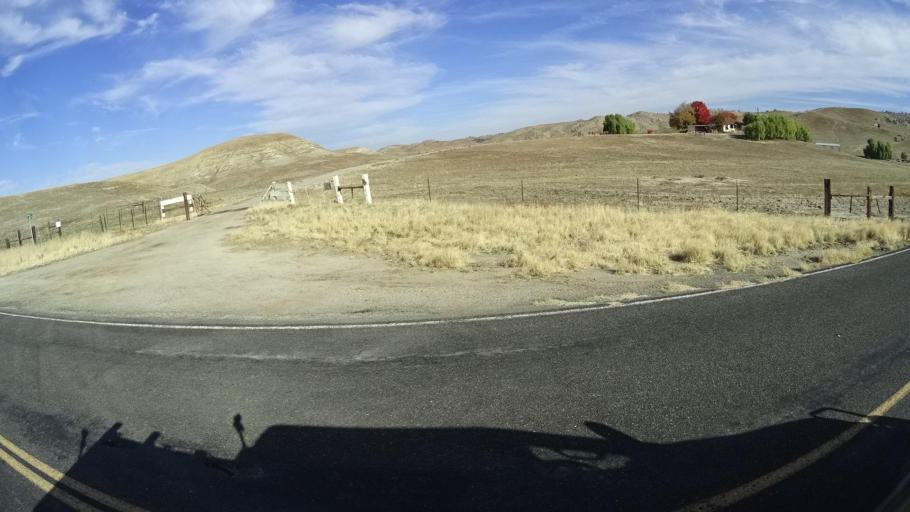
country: US
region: California
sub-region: Kern County
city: Oildale
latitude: 35.6112
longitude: -118.8804
